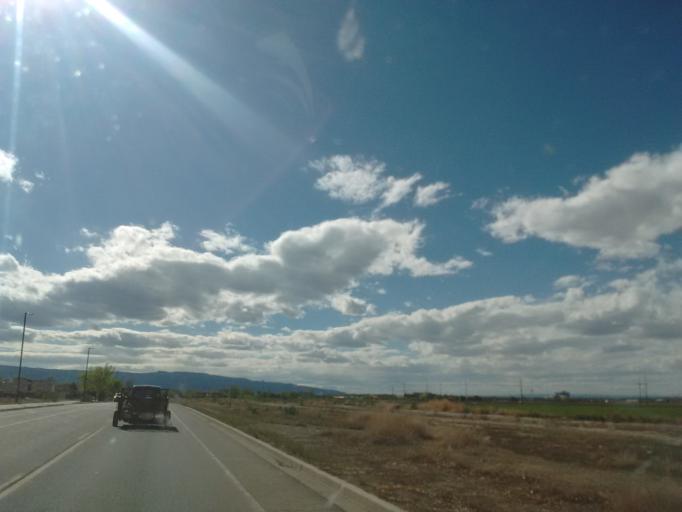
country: US
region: Colorado
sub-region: Mesa County
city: Fruitvale
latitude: 39.0629
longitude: -108.5176
